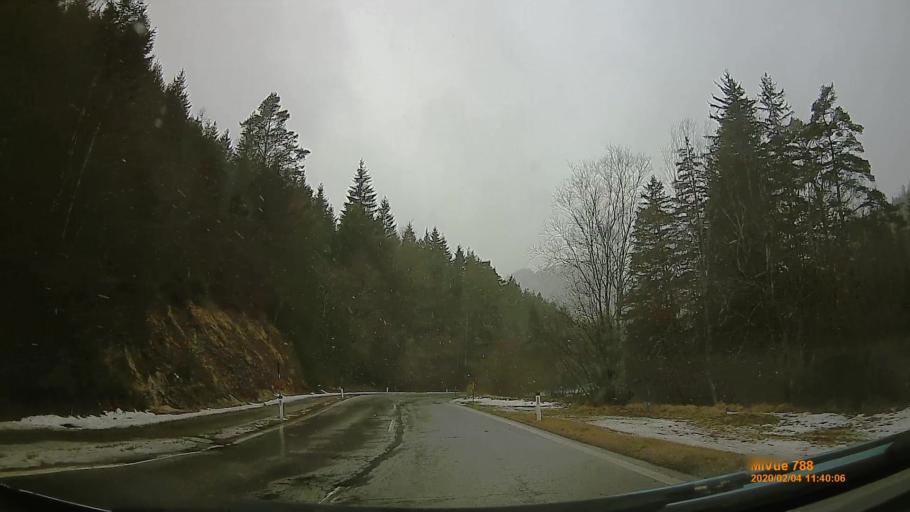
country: AT
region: Styria
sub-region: Politischer Bezirk Bruck-Muerzzuschlag
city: Muerzsteg
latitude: 47.6656
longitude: 15.5148
